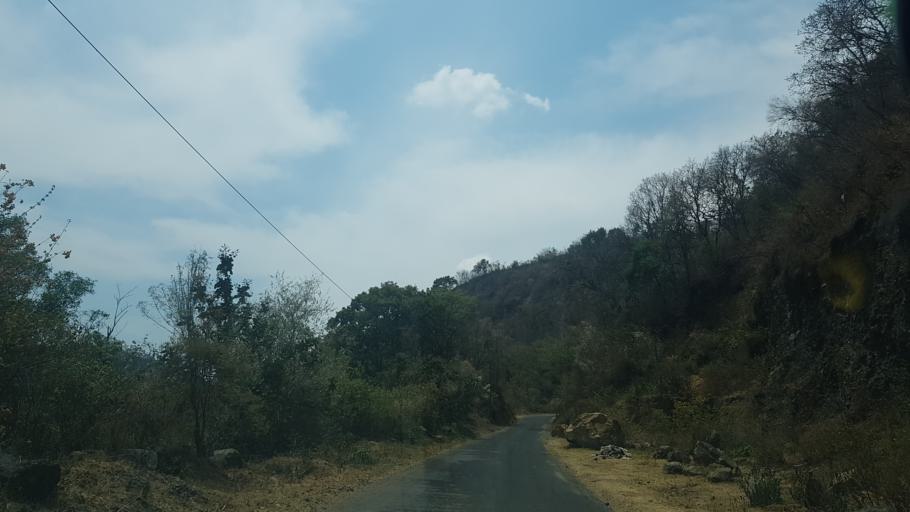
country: MX
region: Puebla
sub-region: Tochimilco
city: La Magdalena Yancuitlalpan
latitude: 18.8766
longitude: -98.6111
